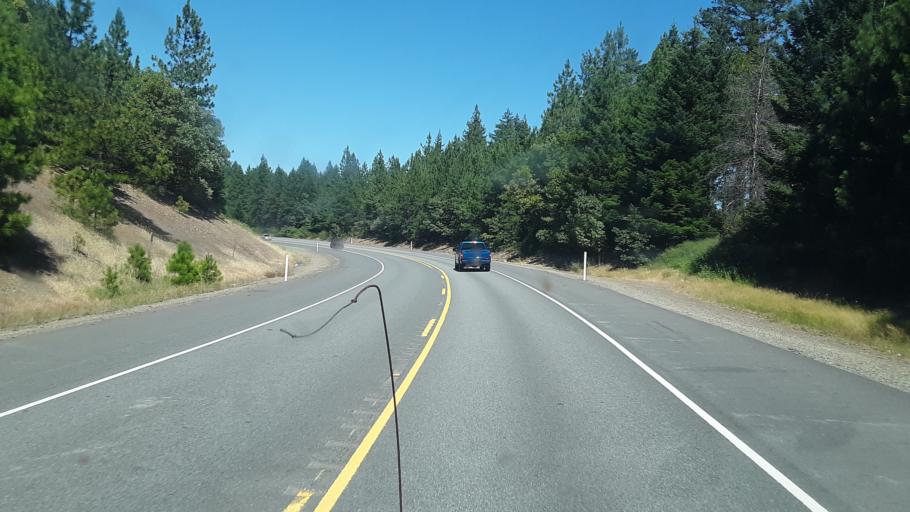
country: US
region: Oregon
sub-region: Josephine County
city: Redwood
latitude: 42.3837
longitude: -123.4683
